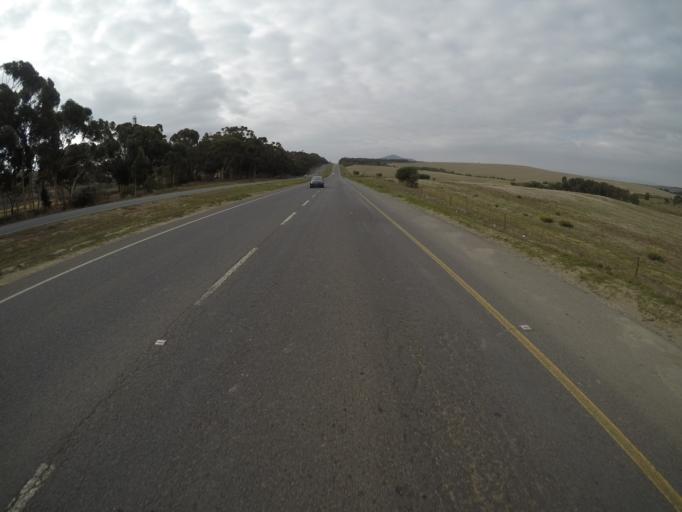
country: ZA
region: Western Cape
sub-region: City of Cape Town
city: Sunset Beach
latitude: -33.7816
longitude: 18.5491
